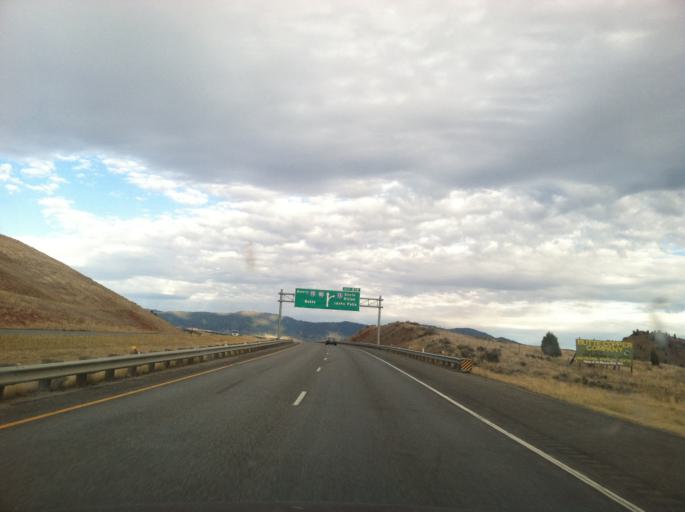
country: US
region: Montana
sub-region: Silver Bow County
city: Butte-Silver Bow (Balance)
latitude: 46.0071
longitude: -112.6574
